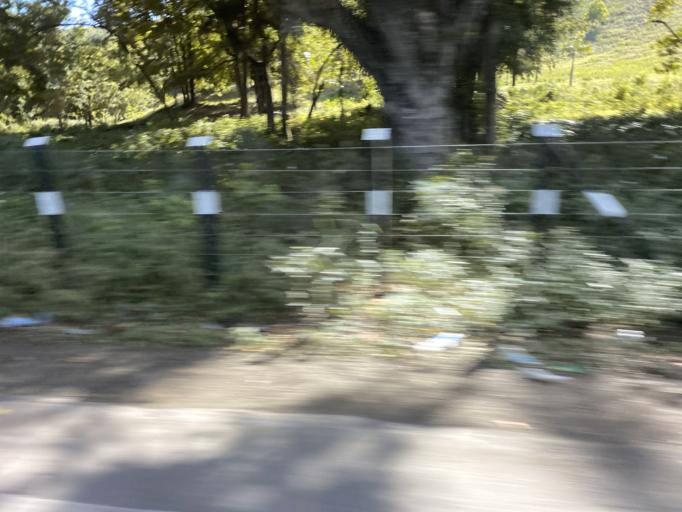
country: DO
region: Espaillat
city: Gaspar Hernandez
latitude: 19.6404
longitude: -70.2557
